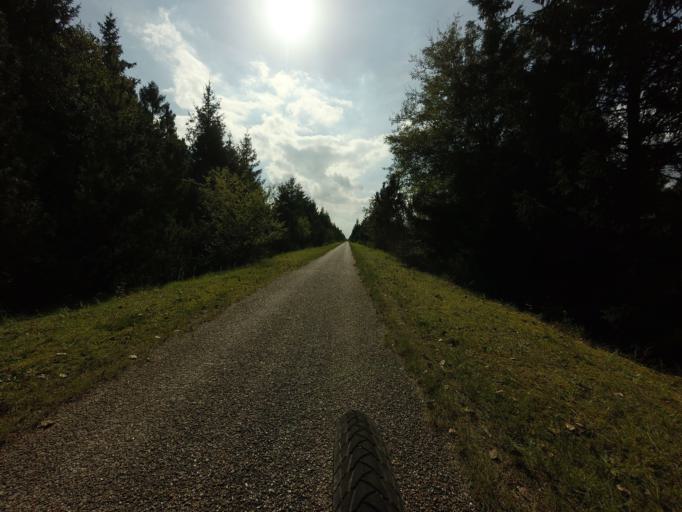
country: DK
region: Central Jutland
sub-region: Viborg Kommune
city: Karup
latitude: 56.2588
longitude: 9.1083
